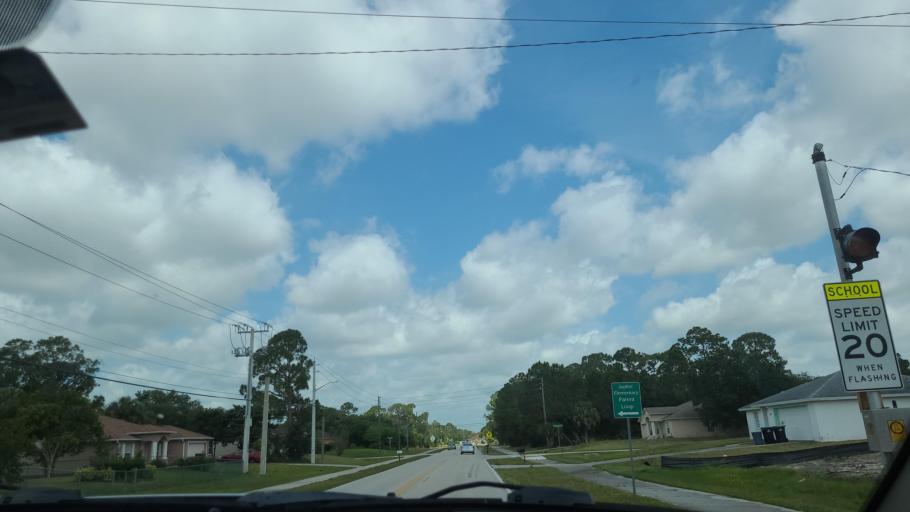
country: US
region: Florida
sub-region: Brevard County
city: June Park
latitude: 27.9901
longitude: -80.6932
